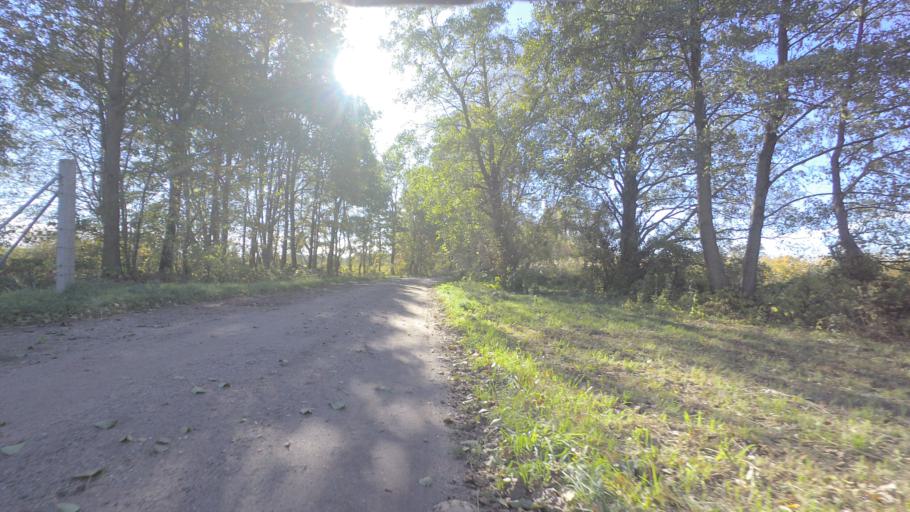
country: DE
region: Saxony
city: Nauwalde
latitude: 51.4376
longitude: 13.3831
